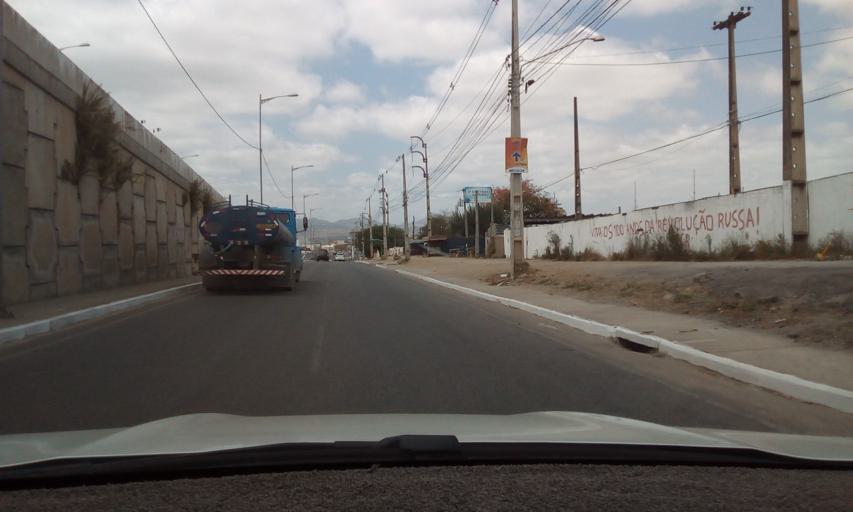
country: BR
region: Pernambuco
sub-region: Caruaru
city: Caruaru
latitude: -8.2677
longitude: -35.9792
